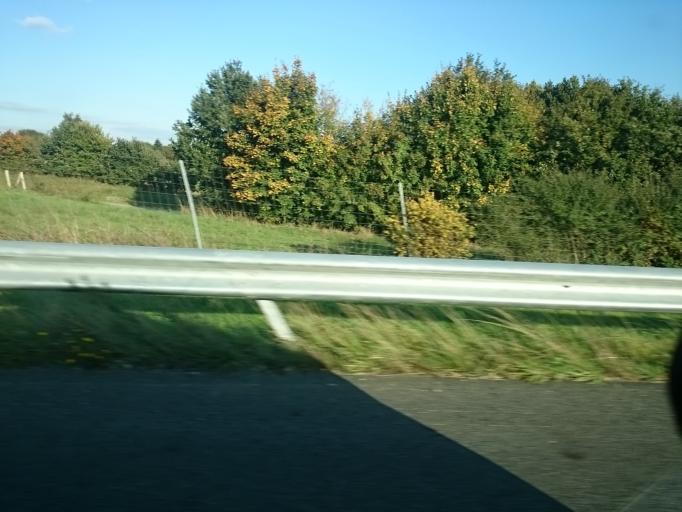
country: FR
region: Brittany
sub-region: Departement d'Ille-et-Vilaine
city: Bain-de-Bretagne
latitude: 47.8735
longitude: -1.6890
